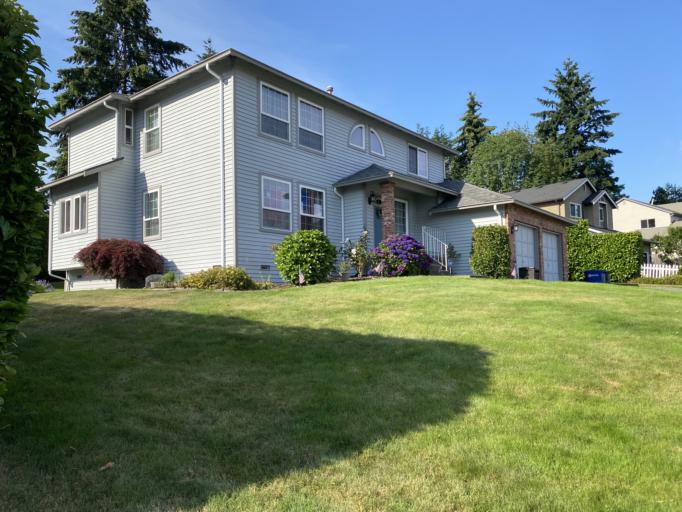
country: US
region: Washington
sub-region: King County
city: Kenmore
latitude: 47.7836
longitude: -122.2375
